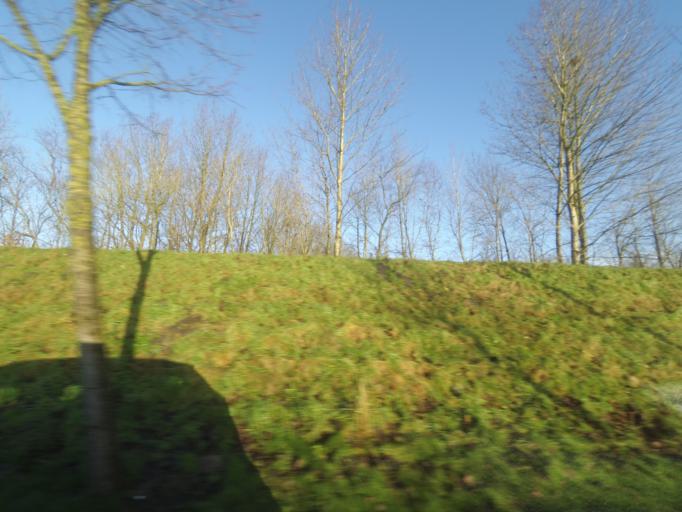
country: DK
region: Central Jutland
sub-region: Ikast-Brande Kommune
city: Ikast
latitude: 56.1187
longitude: 9.1438
